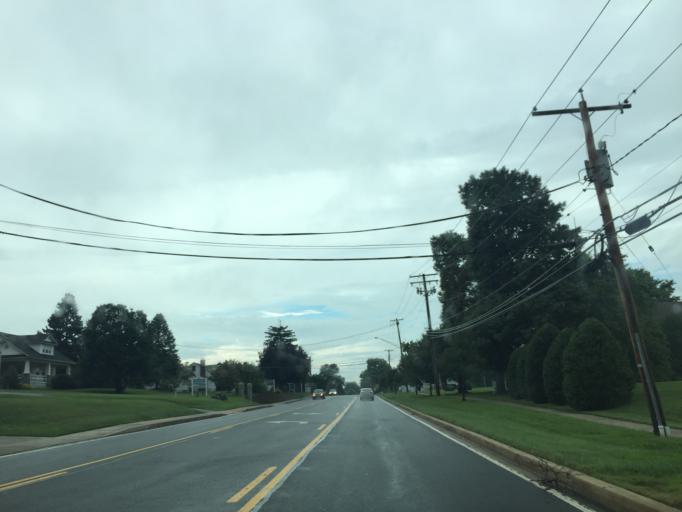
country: US
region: Maryland
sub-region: Harford County
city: South Bel Air
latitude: 39.5299
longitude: -76.3423
